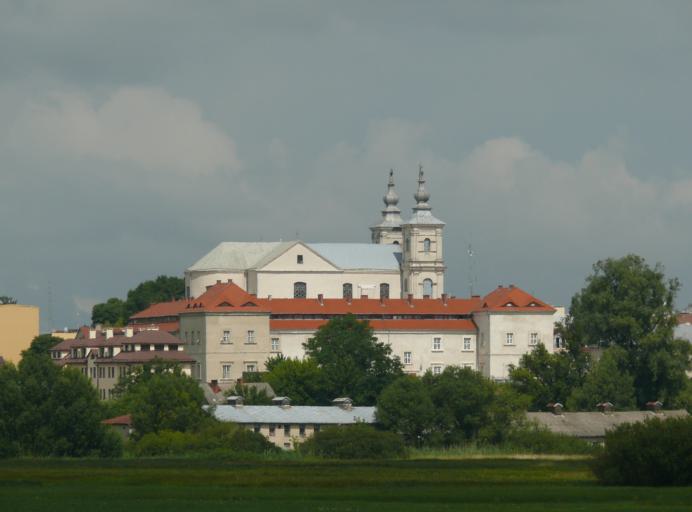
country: PL
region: Lublin Voivodeship
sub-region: Powiat krasnostawski
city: Krasnystaw
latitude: 50.9736
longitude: 23.1690
